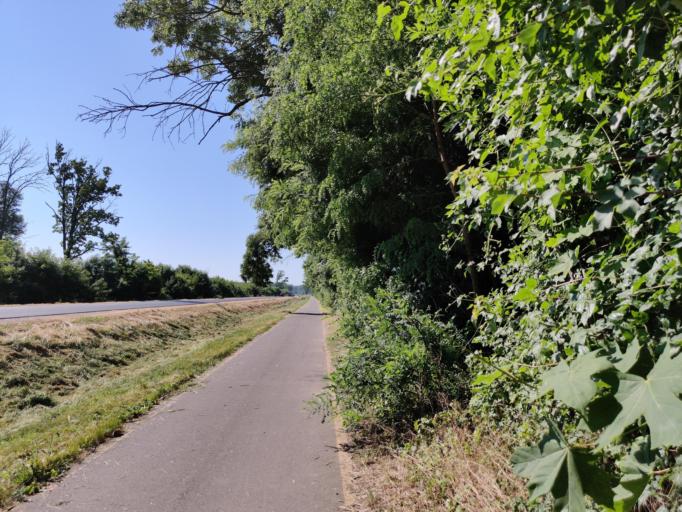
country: HU
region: Hajdu-Bihar
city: Balmazujvaros
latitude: 47.5960
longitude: 21.3394
